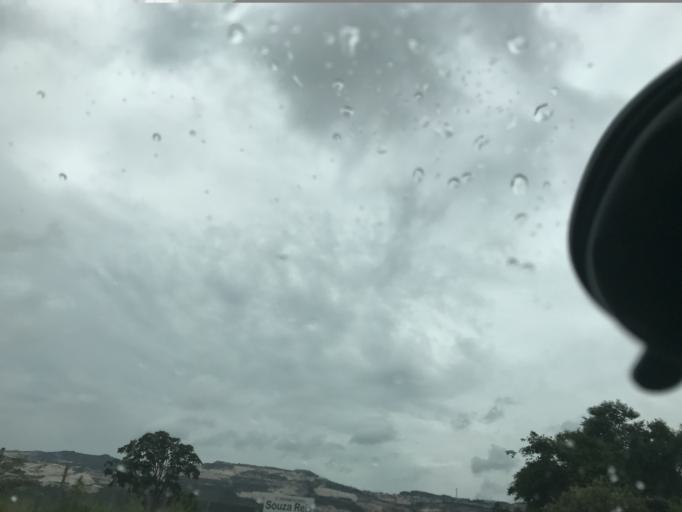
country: BR
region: Minas Gerais
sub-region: Conceicao Do Rio Verde
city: Conceicao do Rio Verde
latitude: -21.6960
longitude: -45.0018
